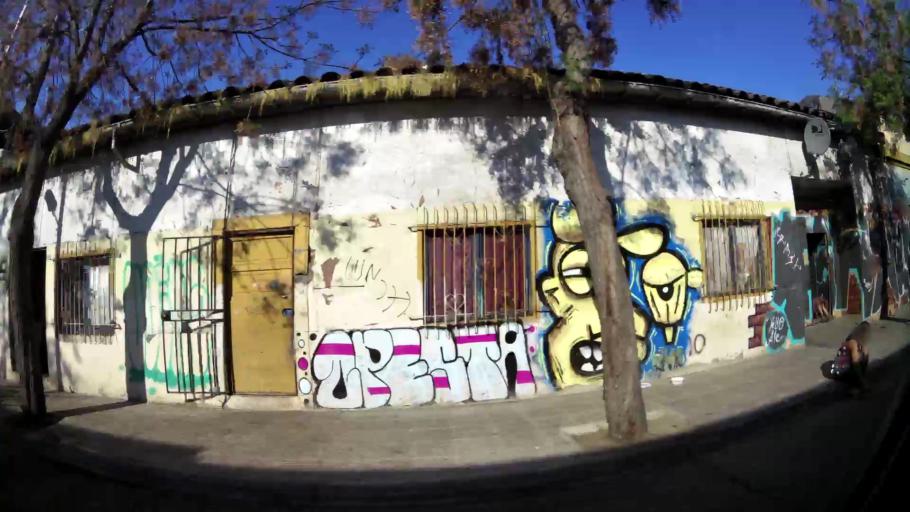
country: CL
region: Santiago Metropolitan
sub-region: Provincia de Santiago
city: Santiago
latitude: -33.4441
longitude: -70.6730
